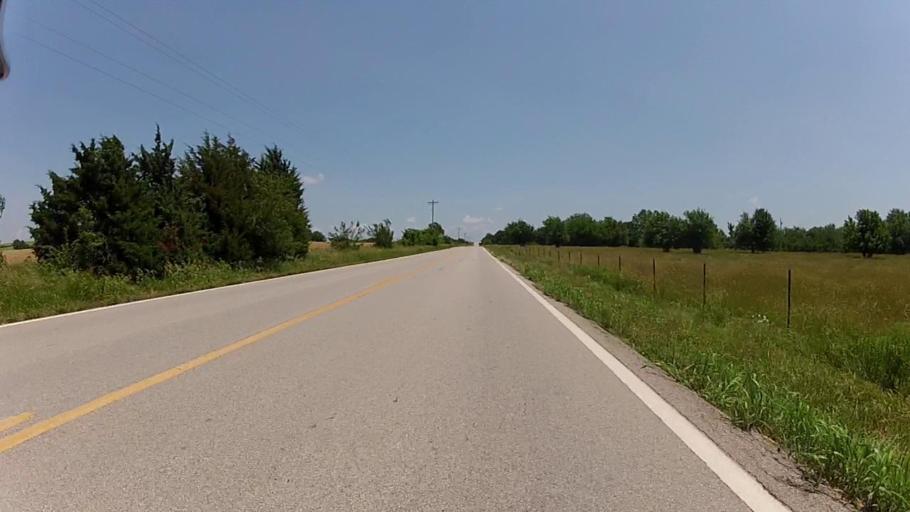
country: US
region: Kansas
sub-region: Montgomery County
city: Cherryvale
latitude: 37.1940
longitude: -95.5106
